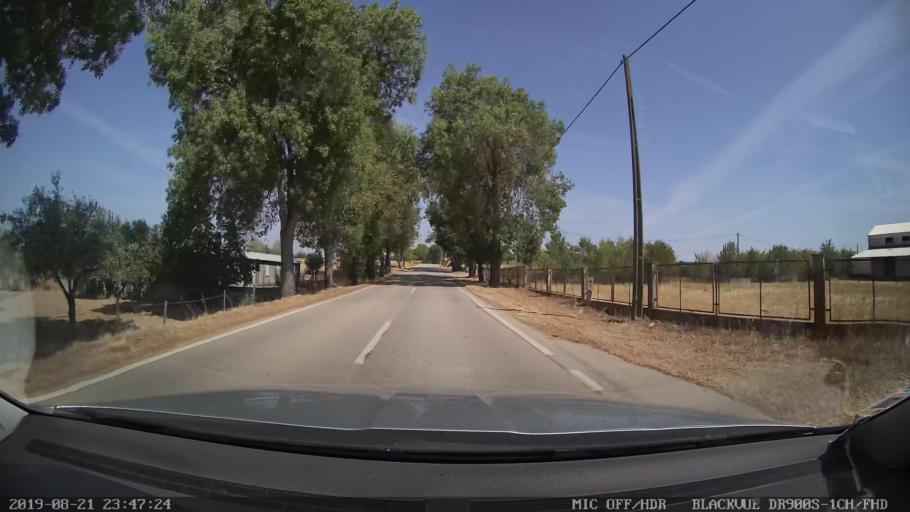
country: PT
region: Castelo Branco
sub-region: Idanha-A-Nova
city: Idanha-a-Nova
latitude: 39.8514
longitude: -7.2573
